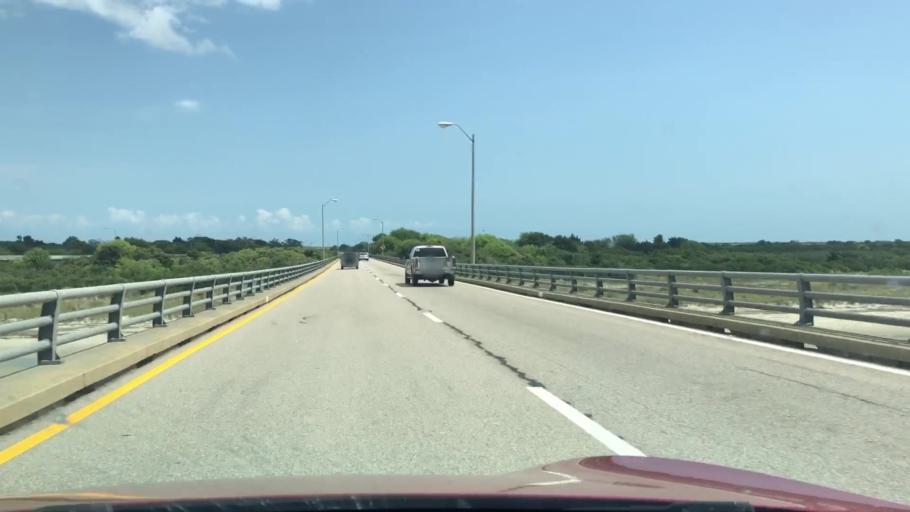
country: US
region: Virginia
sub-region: Northampton County
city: Cape Charles
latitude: 37.0909
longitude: -75.9804
